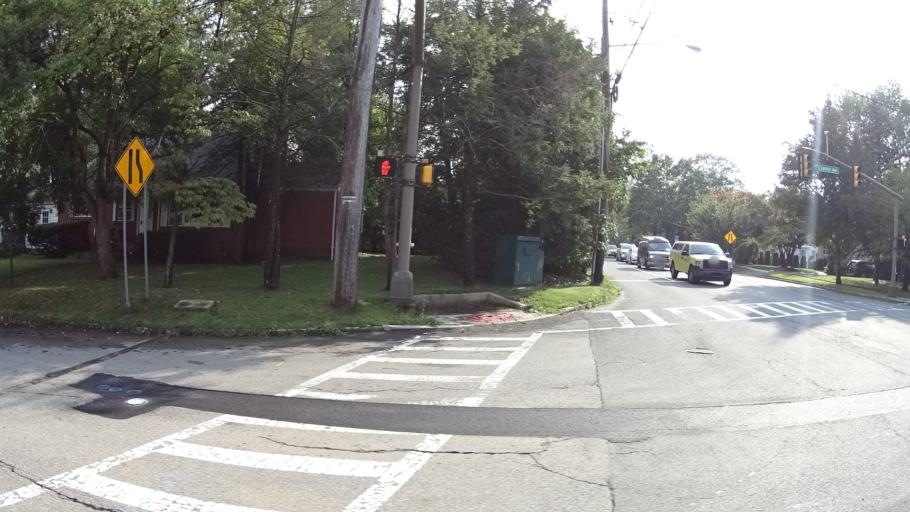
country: US
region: New Jersey
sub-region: Union County
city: New Providence
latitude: 40.6981
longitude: -74.4206
